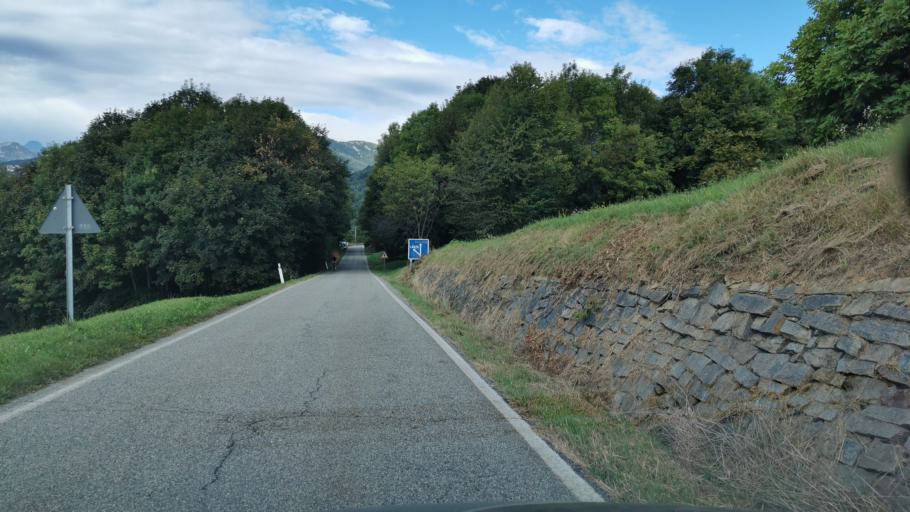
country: IT
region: Piedmont
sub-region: Provincia di Torino
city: Coassolo
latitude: 45.3022
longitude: 7.4845
